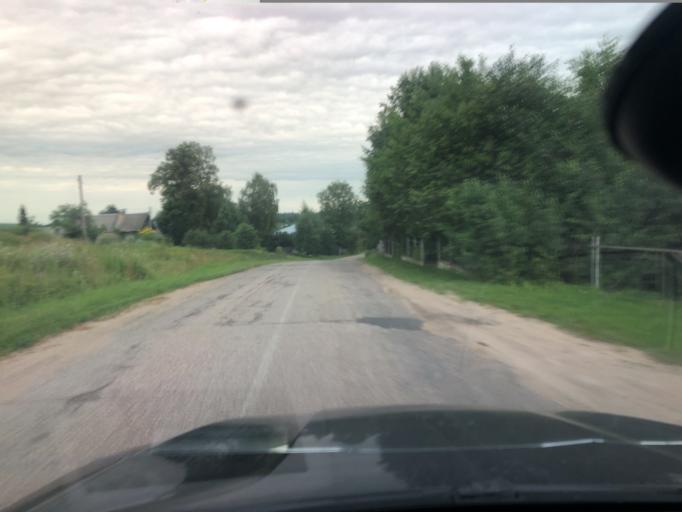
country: RU
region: Jaroslavl
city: Petrovsk
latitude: 57.0098
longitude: 38.9780
